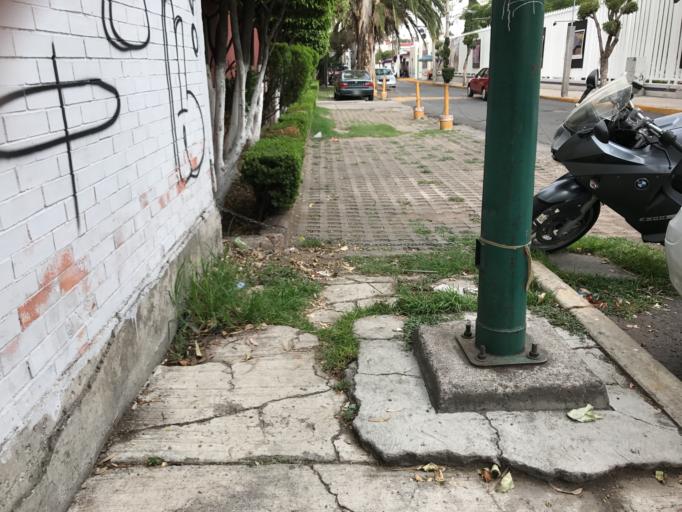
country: MX
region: Mexico City
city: Tlalpan
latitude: 19.2898
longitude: -99.1385
